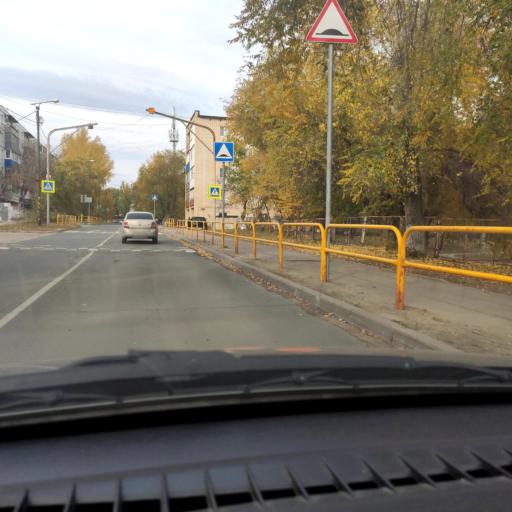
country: RU
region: Samara
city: Zhigulevsk
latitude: 53.4846
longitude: 49.4801
